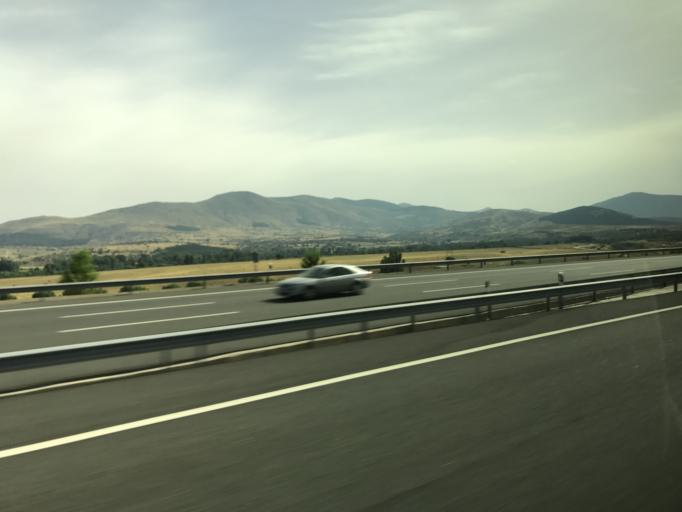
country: ES
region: Castille and Leon
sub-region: Provincia de Segovia
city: Vegas de Matute
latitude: 40.7389
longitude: -4.2197
